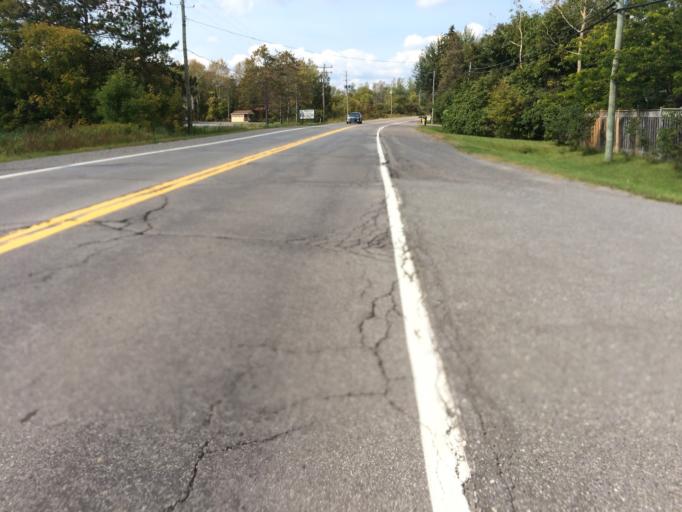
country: CA
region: Ontario
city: Bells Corners
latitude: 45.2091
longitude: -75.6605
